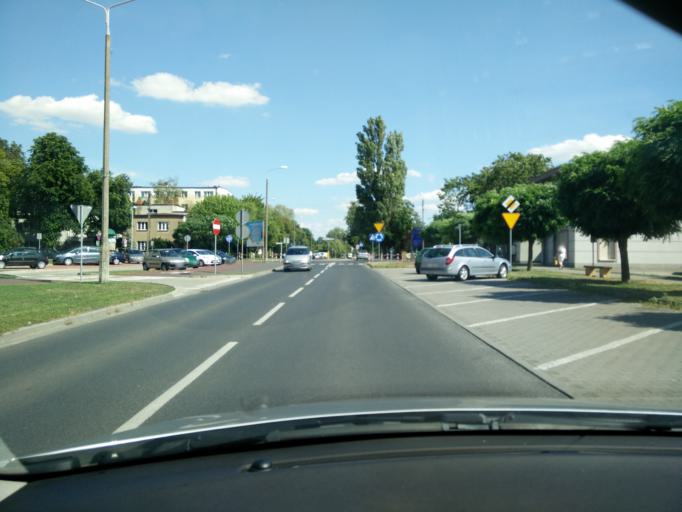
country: PL
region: Greater Poland Voivodeship
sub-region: Powiat sredzki
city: Sroda Wielkopolska
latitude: 52.2247
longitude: 17.2732
